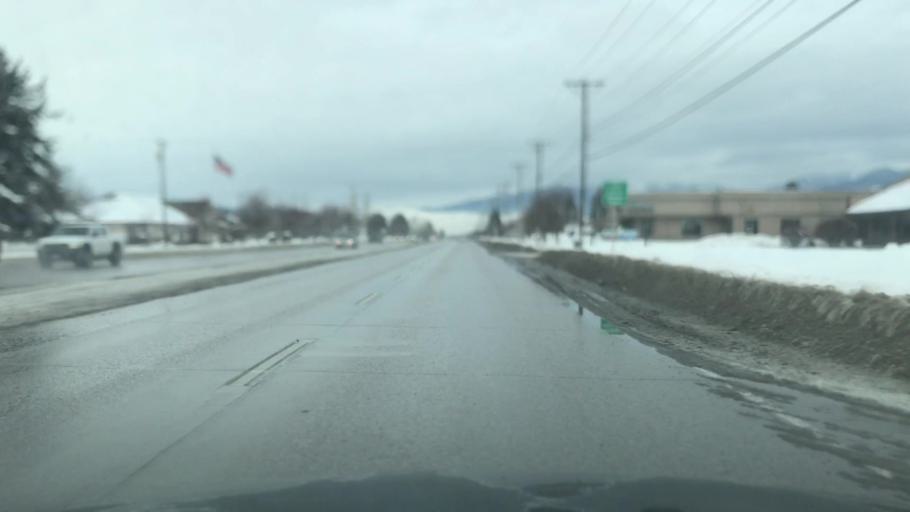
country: US
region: Montana
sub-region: Missoula County
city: Orchard Homes
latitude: 46.8579
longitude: -114.0394
